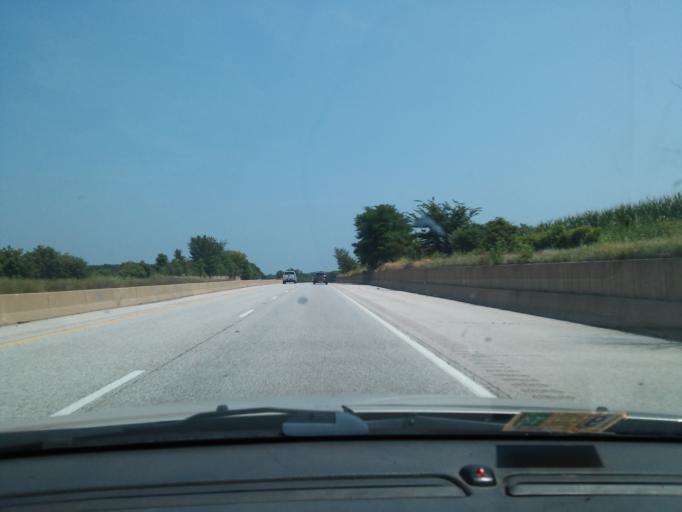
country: US
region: Illinois
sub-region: Pike County
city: Griggsville
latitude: 39.6811
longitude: -90.6689
